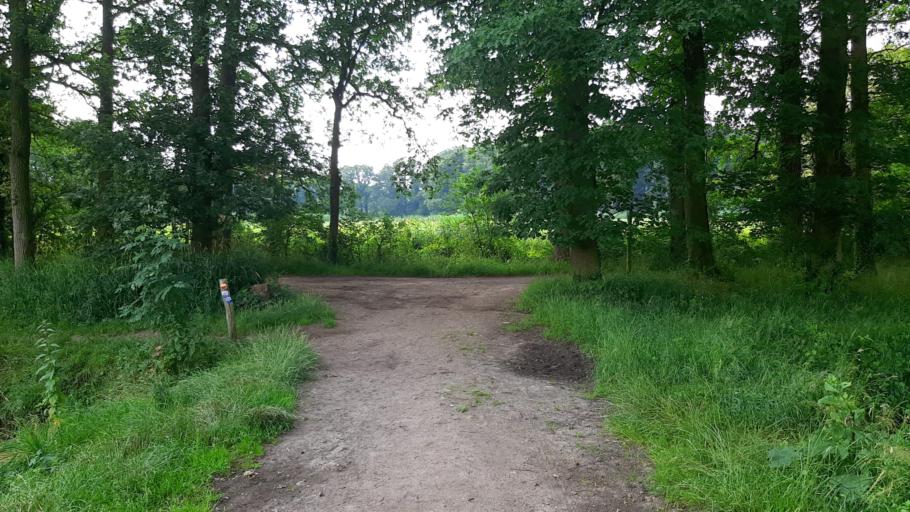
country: NL
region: Gelderland
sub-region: Gemeente Brummen
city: Brummen
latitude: 52.0811
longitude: 6.1348
